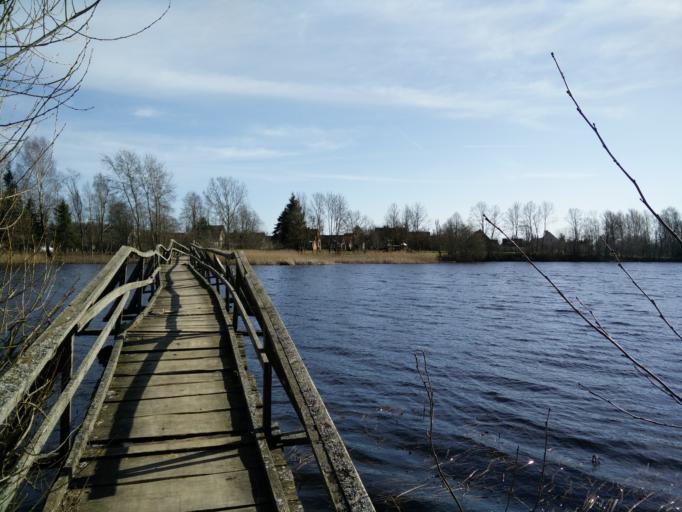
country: LT
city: Ariogala
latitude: 55.3931
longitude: 23.3318
